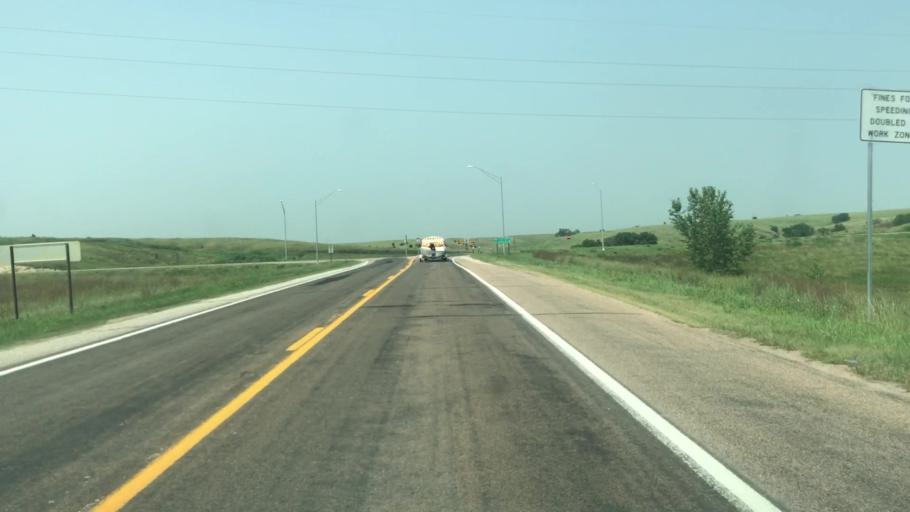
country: US
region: Nebraska
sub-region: Sherman County
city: Loup City
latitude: 41.2614
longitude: -98.9388
